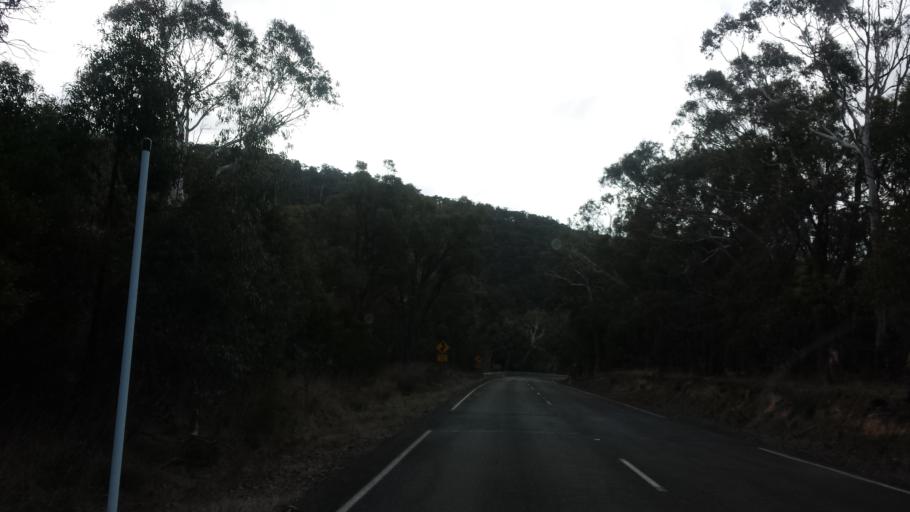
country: AU
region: Victoria
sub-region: Alpine
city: Mount Beauty
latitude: -37.1201
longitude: 147.5439
